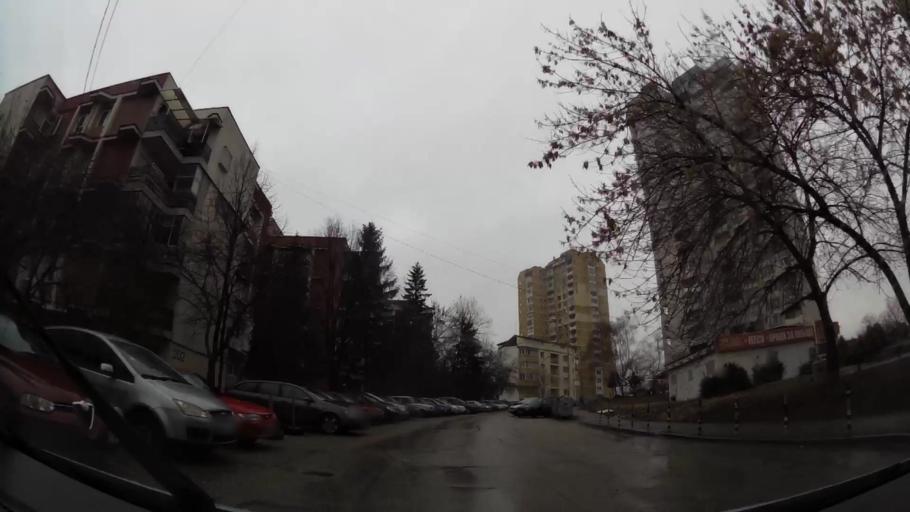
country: BG
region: Sofia-Capital
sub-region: Stolichna Obshtina
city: Sofia
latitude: 42.6385
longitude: 23.3697
